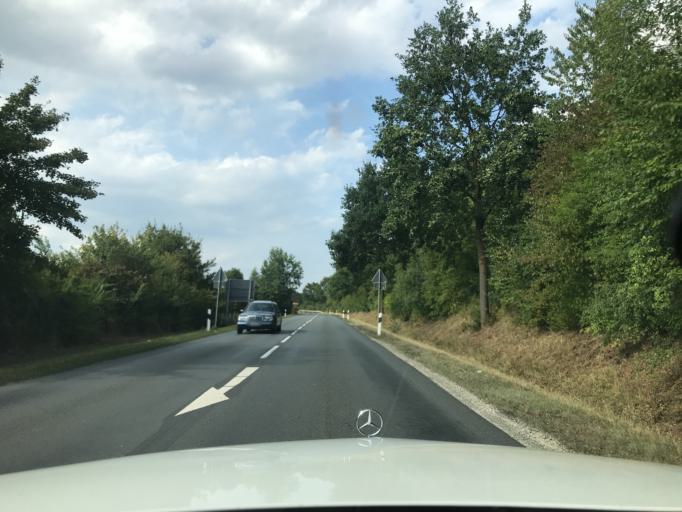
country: DE
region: Lower Saxony
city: Adelebsen
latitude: 51.5811
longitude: 9.7652
